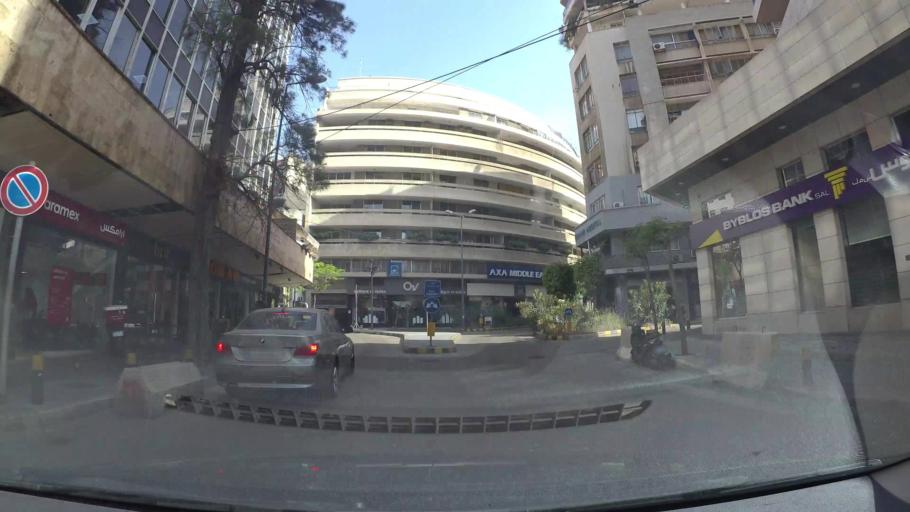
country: LB
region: Beyrouth
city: Ra's Bayrut
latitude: 33.8978
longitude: 35.4888
